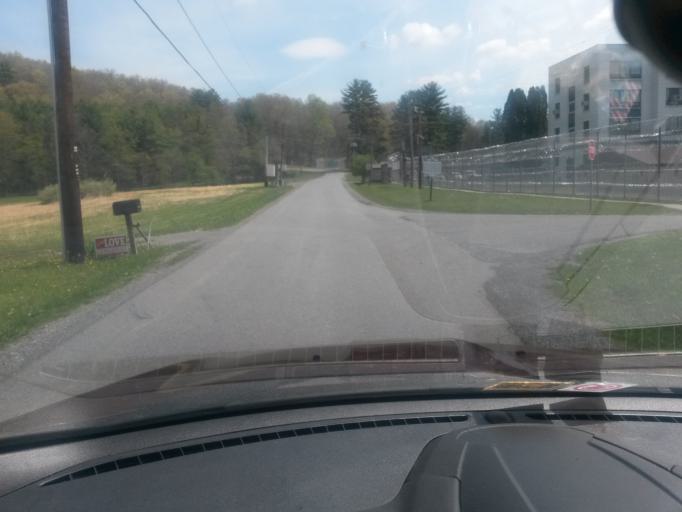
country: US
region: West Virginia
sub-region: Pocahontas County
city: Marlinton
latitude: 38.0862
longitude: -80.2223
